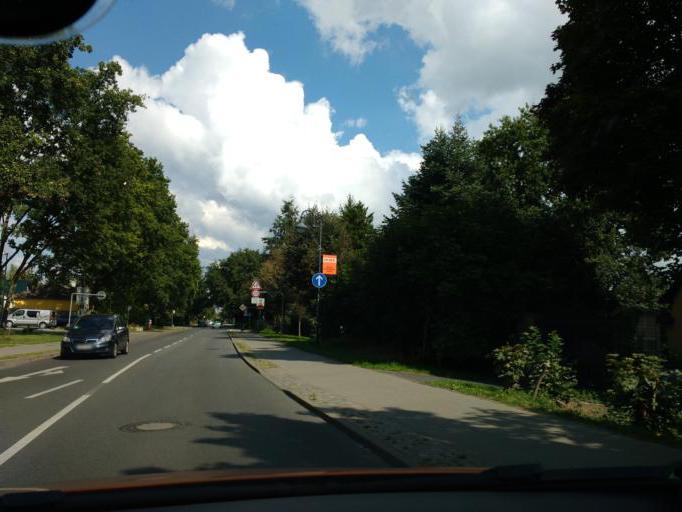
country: DE
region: Brandenburg
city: Wandlitz
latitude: 52.7470
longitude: 13.4639
